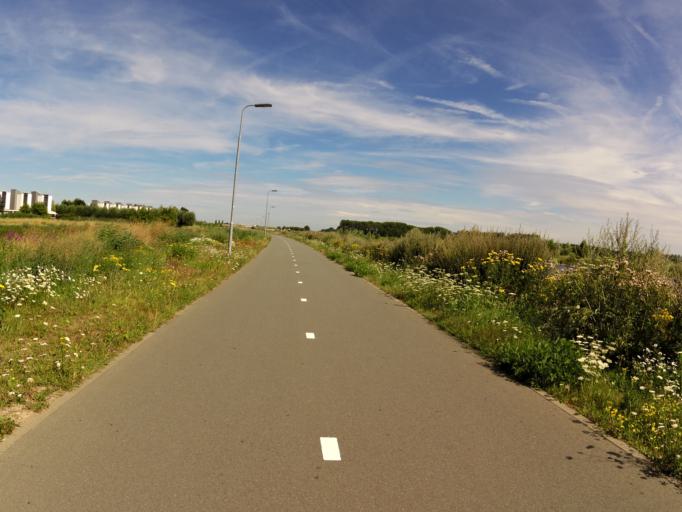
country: NL
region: North Brabant
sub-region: Gemeente 's-Hertogenbosch
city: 's-Hertogenbosch
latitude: 51.7319
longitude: 5.3382
